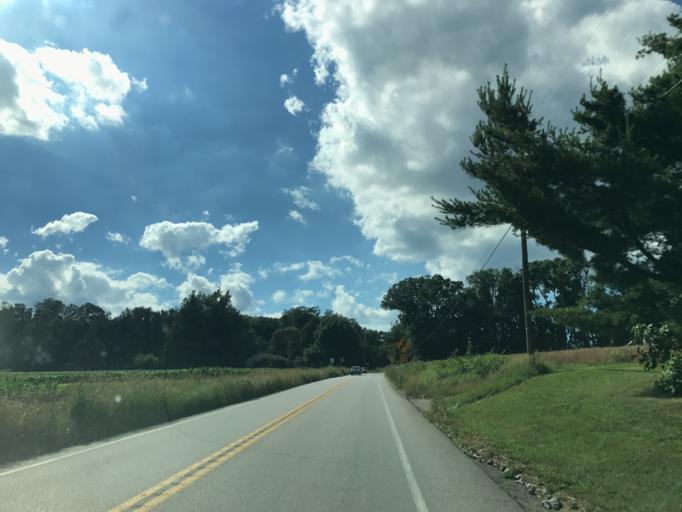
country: US
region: Pennsylvania
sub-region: York County
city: Glen Rock
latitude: 39.7433
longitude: -76.7999
